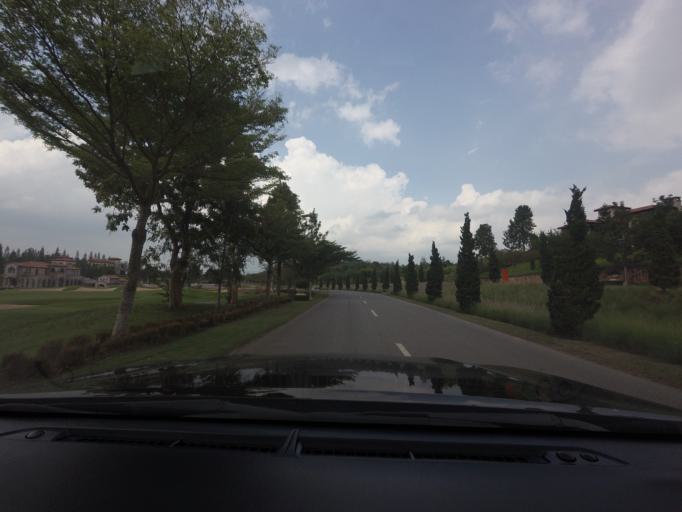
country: TH
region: Nakhon Ratchasima
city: Pak Chong
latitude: 14.5089
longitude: 101.5048
